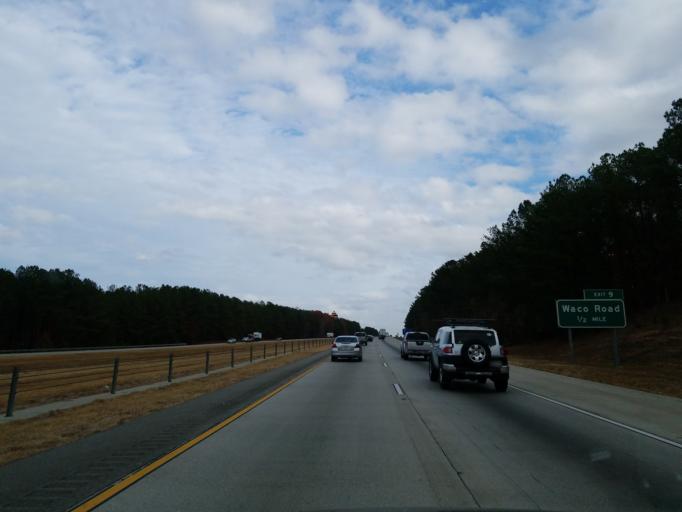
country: US
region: Georgia
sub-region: Carroll County
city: Mount Zion
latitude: 33.6896
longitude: -85.2013
